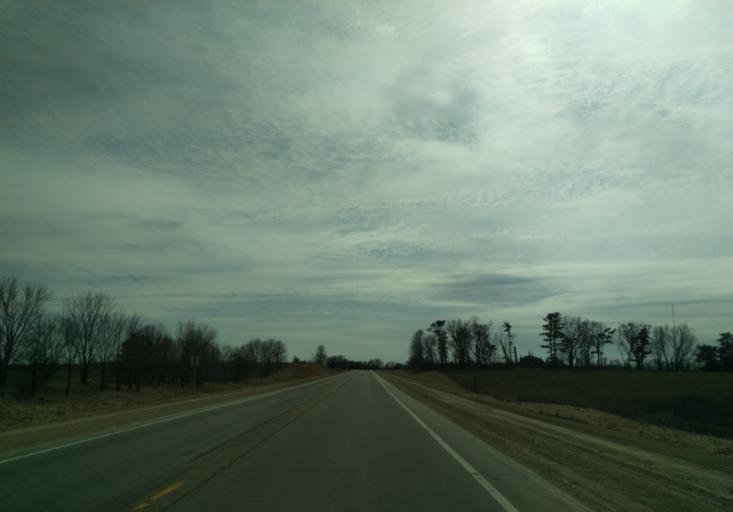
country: US
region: Iowa
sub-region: Winneshiek County
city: Decorah
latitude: 43.3520
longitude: -91.8052
